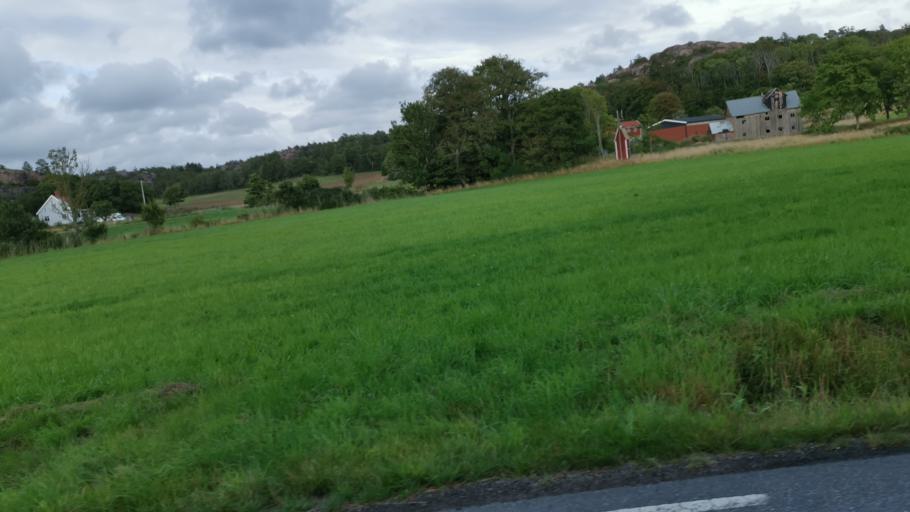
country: SE
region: Vaestra Goetaland
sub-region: Sotenas Kommun
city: Hunnebostrand
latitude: 58.5198
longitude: 11.3031
